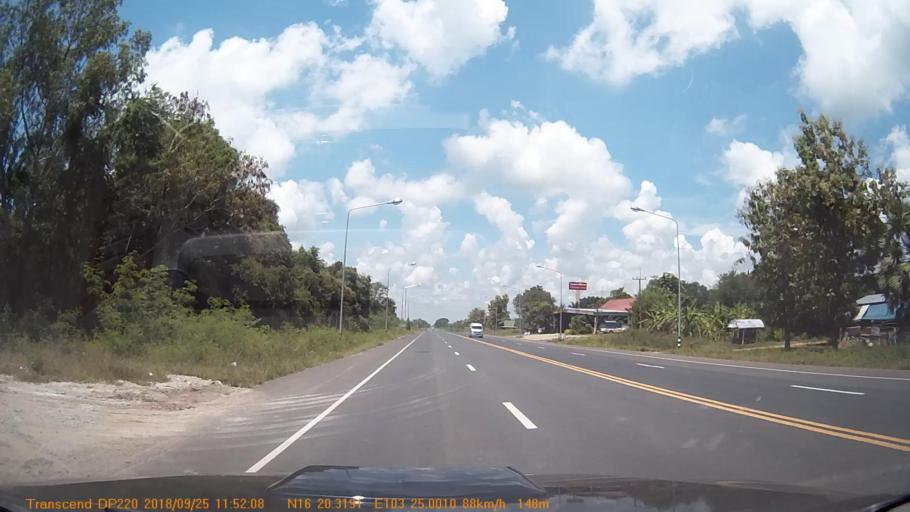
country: TH
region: Kalasin
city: Yang Talat
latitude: 16.3388
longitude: 103.4165
